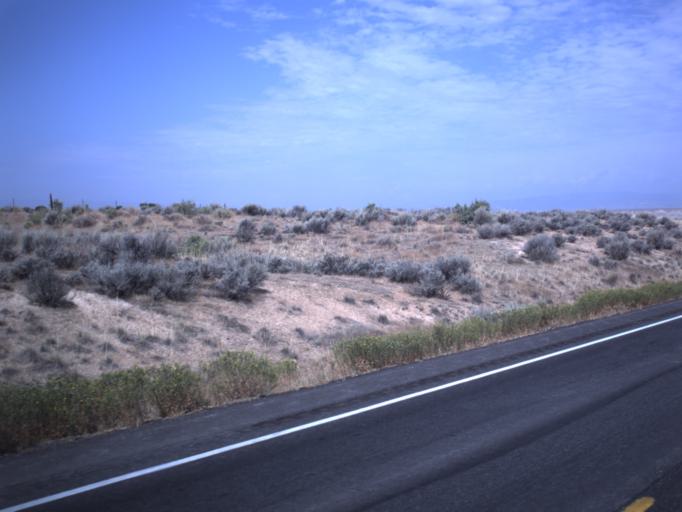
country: US
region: Utah
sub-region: Uintah County
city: Naples
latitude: 40.3556
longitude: -109.3123
